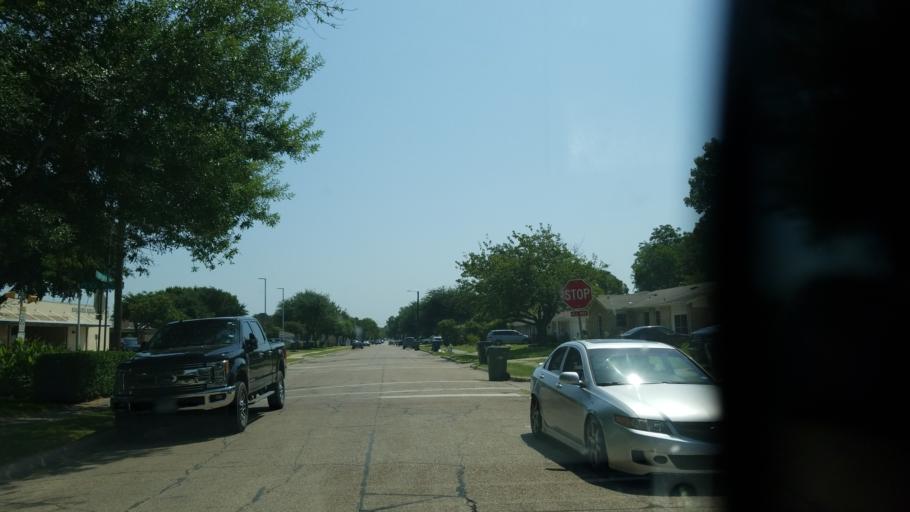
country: US
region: Texas
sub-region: Dallas County
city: Garland
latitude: 32.9175
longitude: -96.6239
